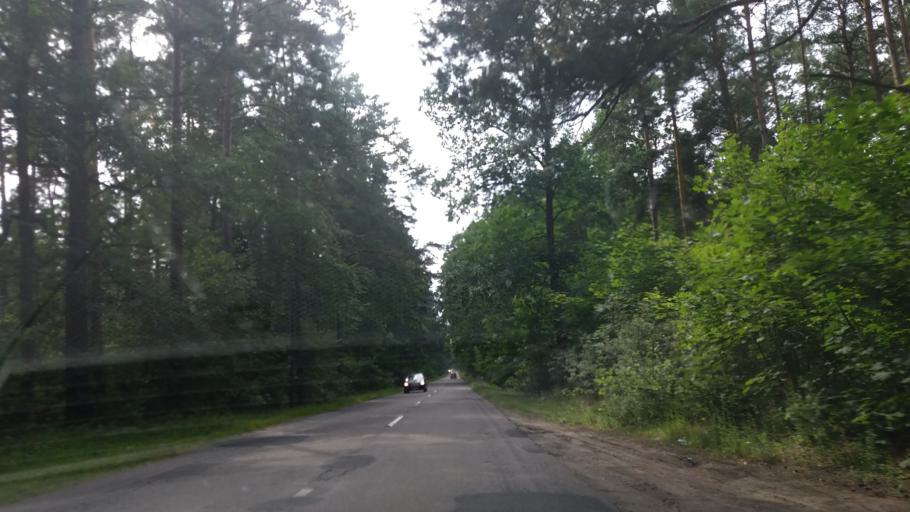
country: PL
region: Lubusz
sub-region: Powiat strzelecko-drezdenecki
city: Stare Kurowo
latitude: 52.7412
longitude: 15.6470
